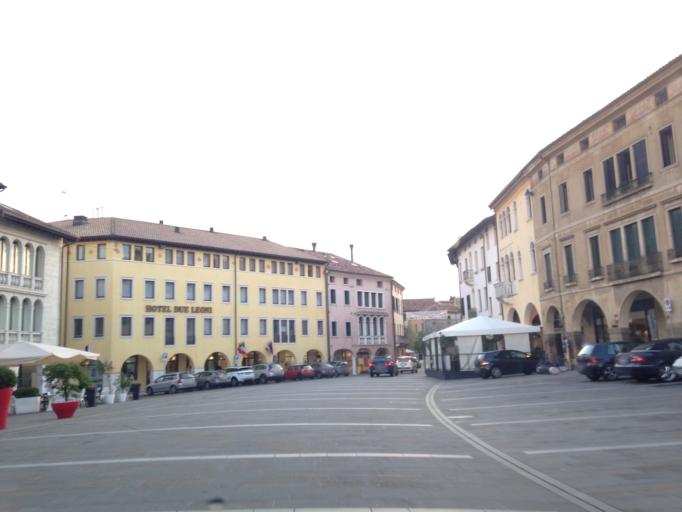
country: IT
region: Friuli Venezia Giulia
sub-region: Provincia di Pordenone
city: Sacile
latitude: 45.9542
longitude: 12.5029
